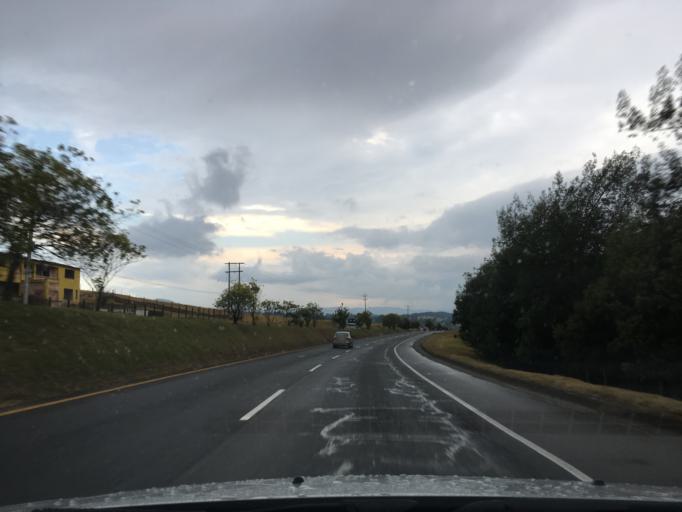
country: CO
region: Cundinamarca
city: Choconta
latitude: 5.1218
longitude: -73.6960
